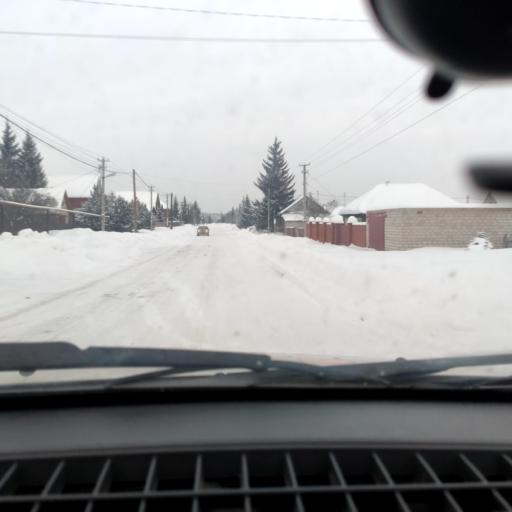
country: RU
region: Bashkortostan
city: Ufa
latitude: 54.5368
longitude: 55.9134
